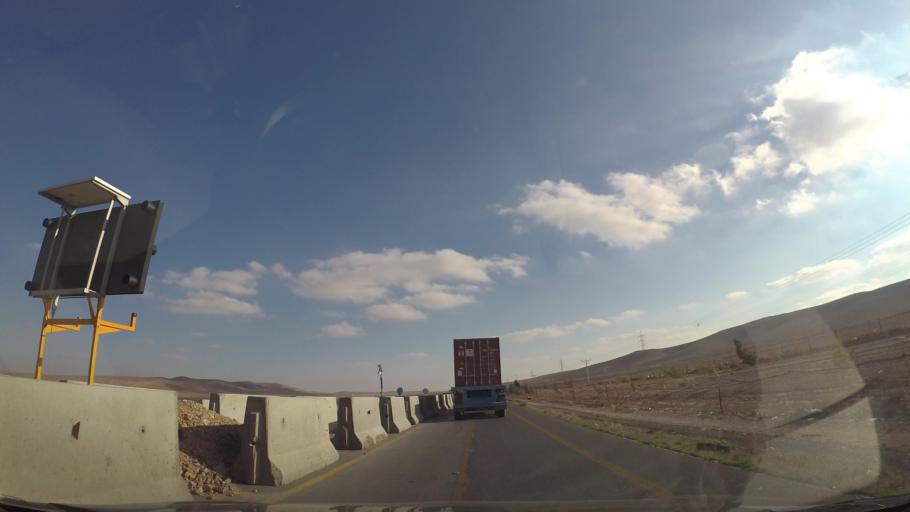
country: JO
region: Karak
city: Adir
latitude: 31.1916
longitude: 36.0175
